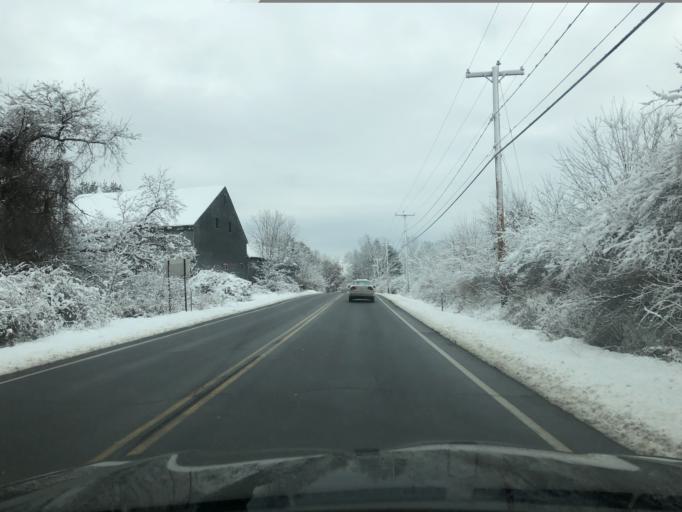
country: US
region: New Hampshire
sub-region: Strafford County
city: Dover
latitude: 43.2241
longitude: -70.8627
